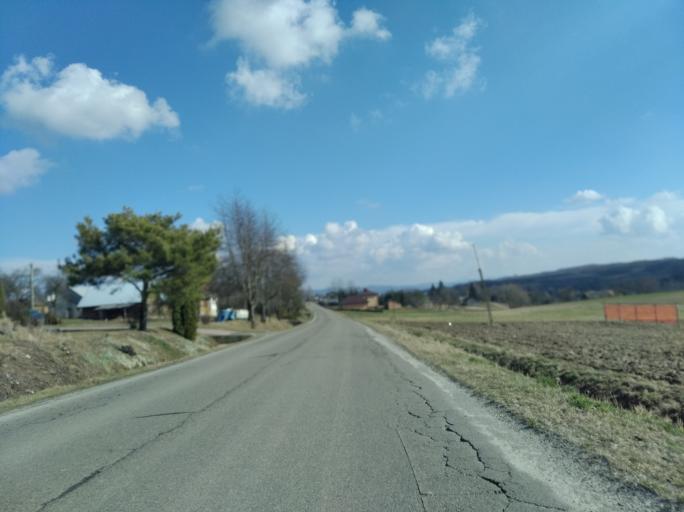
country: PL
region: Subcarpathian Voivodeship
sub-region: Powiat strzyzowski
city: Frysztak
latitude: 49.8499
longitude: 21.5325
